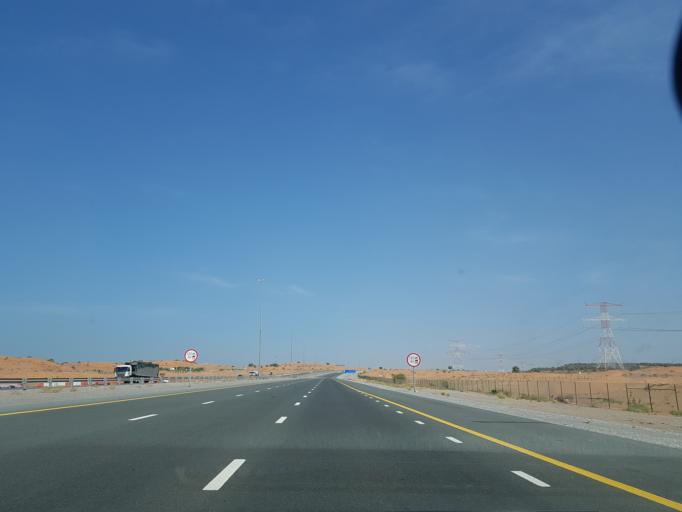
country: AE
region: Ra's al Khaymah
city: Ras al-Khaimah
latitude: 25.6683
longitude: 55.8967
